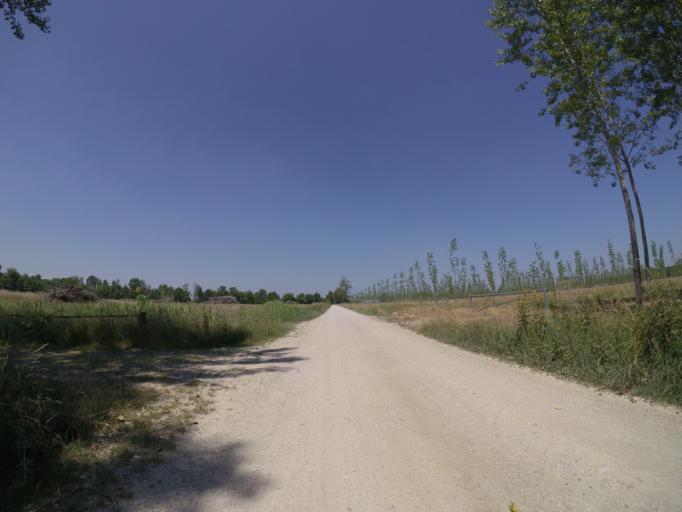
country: IT
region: Friuli Venezia Giulia
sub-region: Provincia di Udine
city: Bertiolo
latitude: 45.9340
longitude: 13.0186
